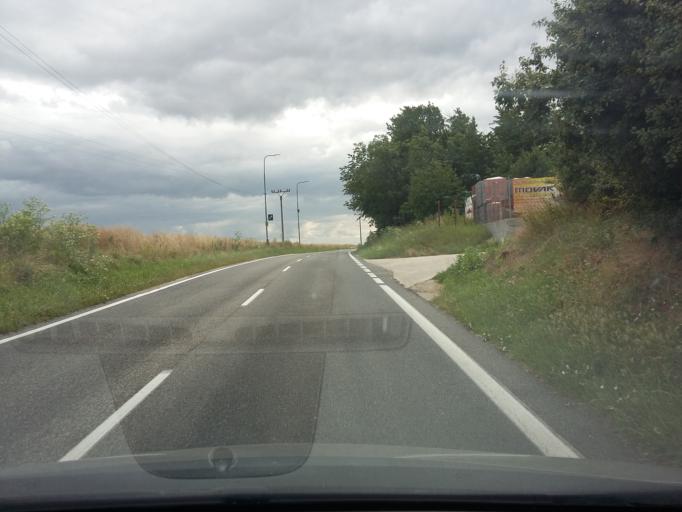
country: SK
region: Trnavsky
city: Vrbove
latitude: 48.6114
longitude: 17.7162
